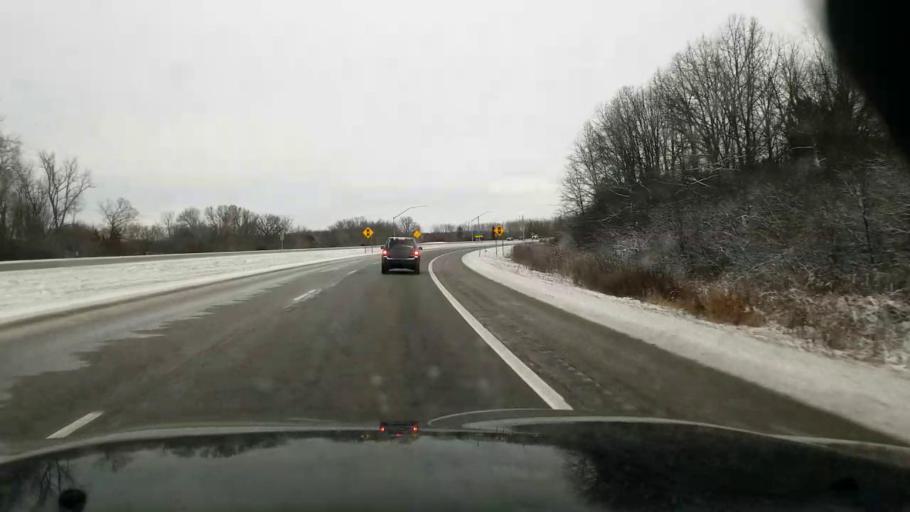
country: US
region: Michigan
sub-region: Jackson County
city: Jackson
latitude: 42.2282
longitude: -84.4761
